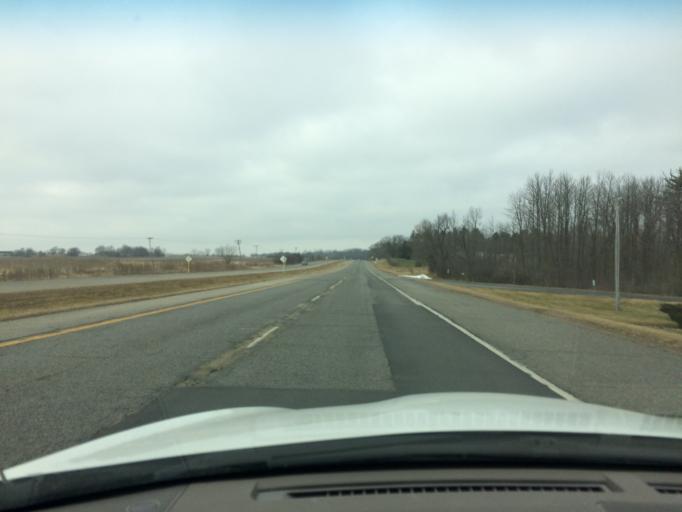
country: US
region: Illinois
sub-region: Kane County
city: Sugar Grove
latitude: 41.7802
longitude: -88.4443
